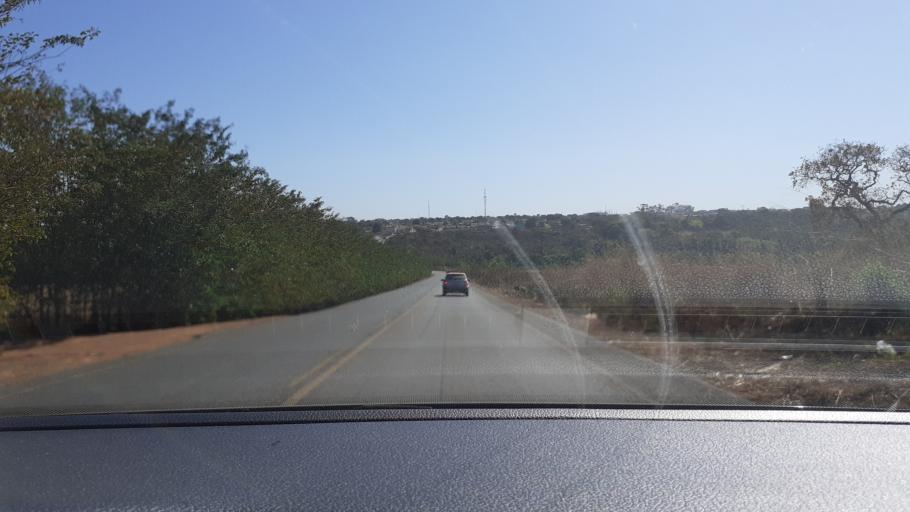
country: BR
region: Goias
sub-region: Aparecida De Goiania
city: Aparecida de Goiania
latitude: -16.8525
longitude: -49.2546
